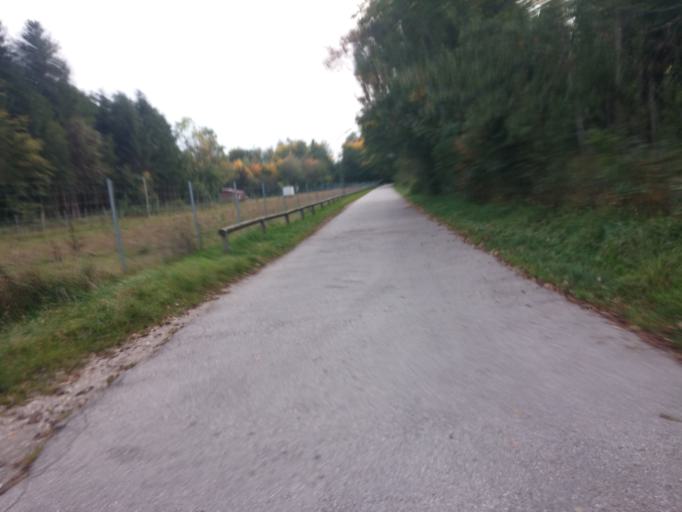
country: DE
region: Bavaria
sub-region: Upper Bavaria
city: Vaterstetten
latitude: 48.0904
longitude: 11.7607
